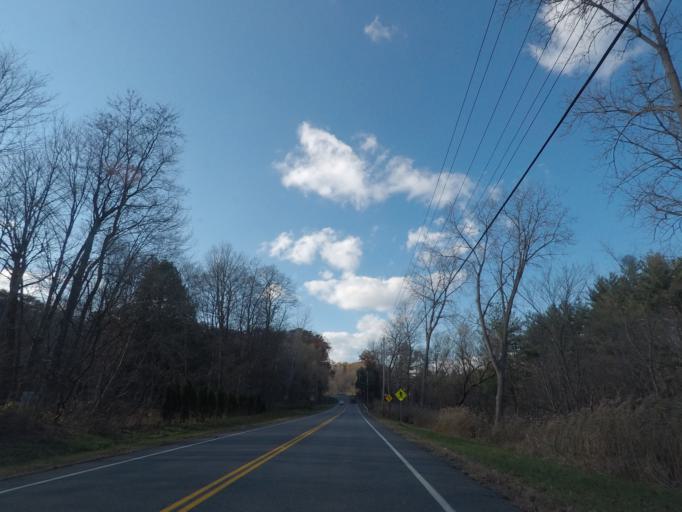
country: US
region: New York
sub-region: Saratoga County
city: Country Knolls
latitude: 42.8883
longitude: -73.8038
